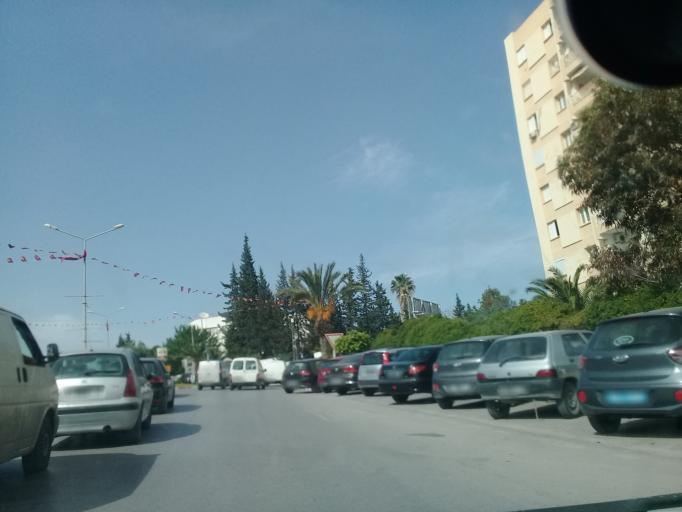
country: TN
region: Ariana
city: Ariana
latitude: 36.8484
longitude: 10.1691
